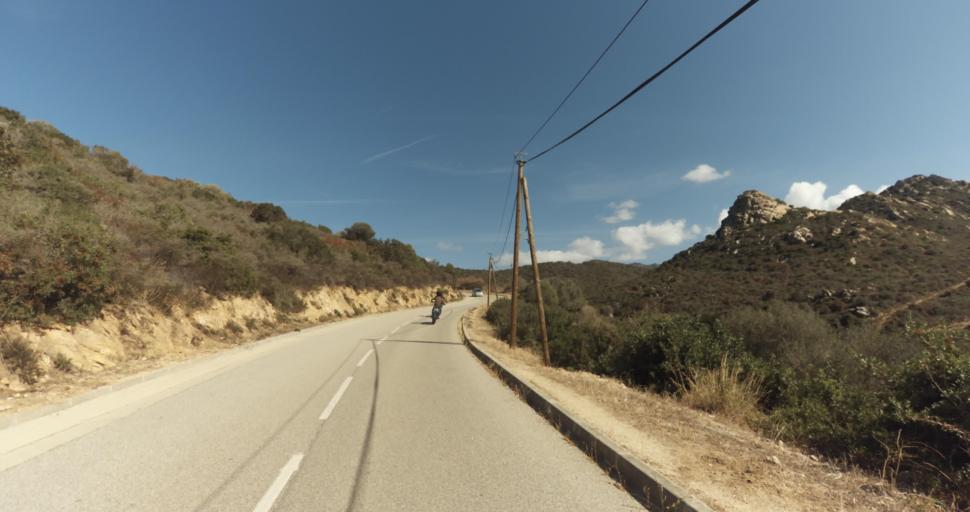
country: FR
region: Corsica
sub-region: Departement de la Corse-du-Sud
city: Ajaccio
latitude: 41.9147
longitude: 8.6439
